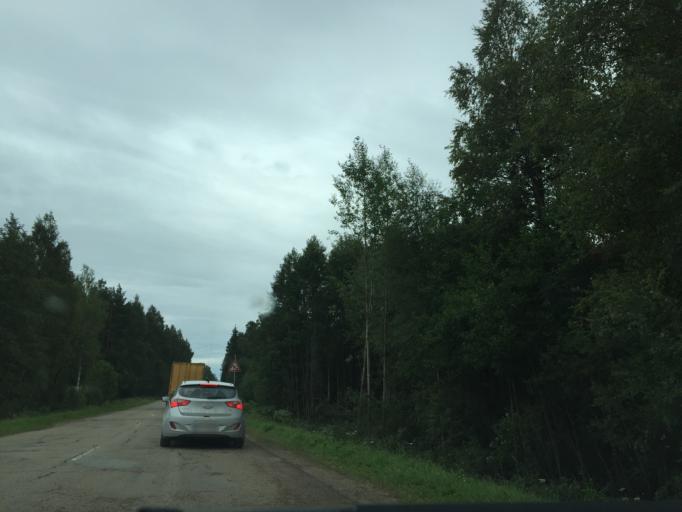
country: LV
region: Preilu Rajons
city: Jaunaglona
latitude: 56.2045
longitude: 26.8715
